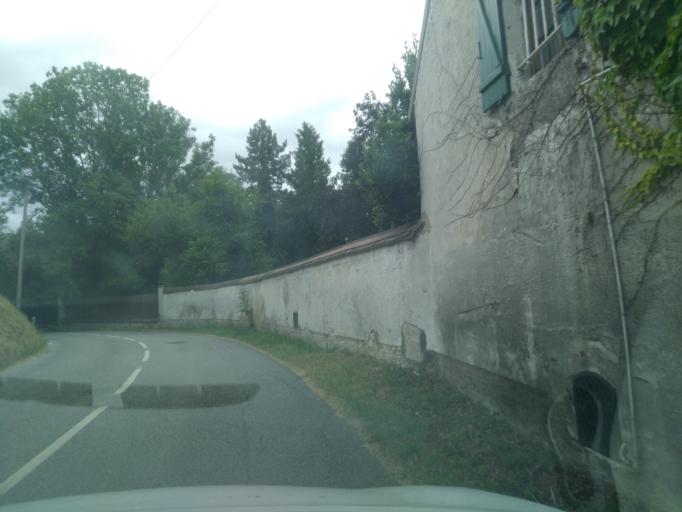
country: FR
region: Ile-de-France
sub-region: Departement des Yvelines
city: Thiverval-Grignon
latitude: 48.8624
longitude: 1.9113
